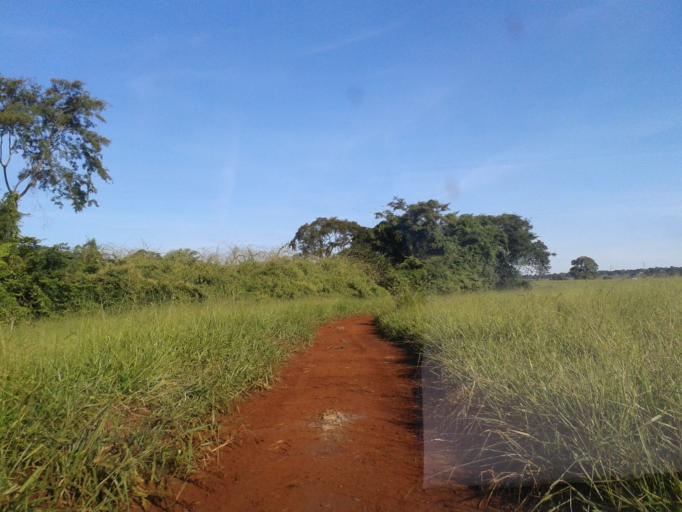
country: BR
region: Minas Gerais
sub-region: Santa Vitoria
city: Santa Vitoria
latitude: -18.9911
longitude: -50.3509
